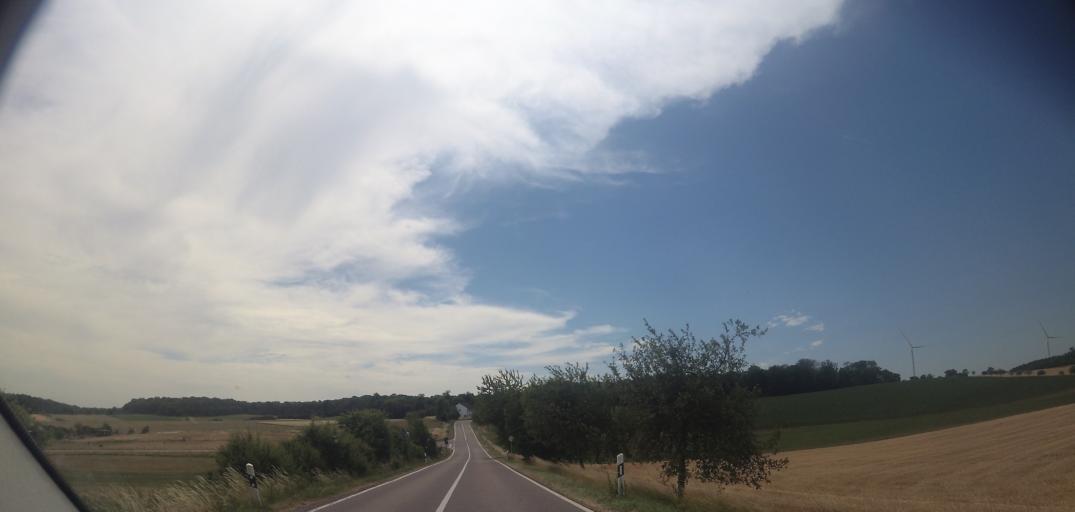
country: DE
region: Saarland
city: Mettlach
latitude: 49.4291
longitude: 6.5543
